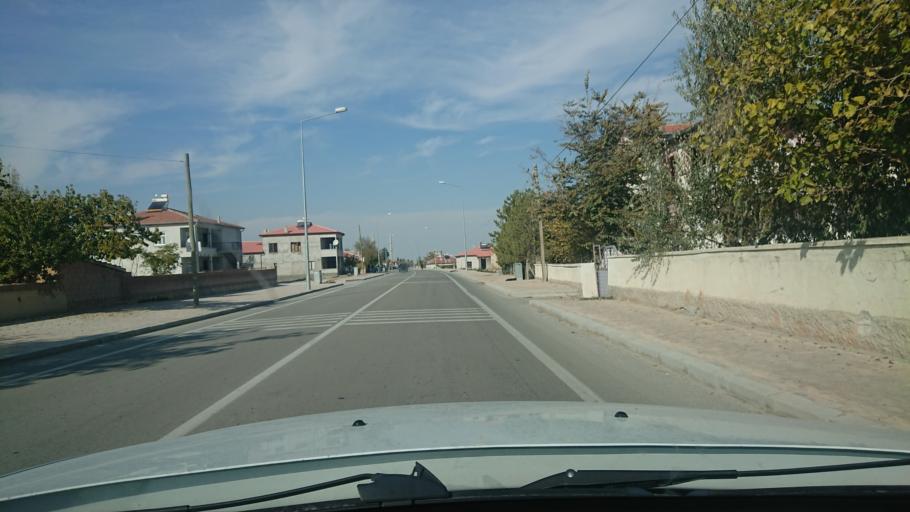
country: TR
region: Aksaray
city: Sultanhani
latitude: 38.2533
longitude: 33.4486
